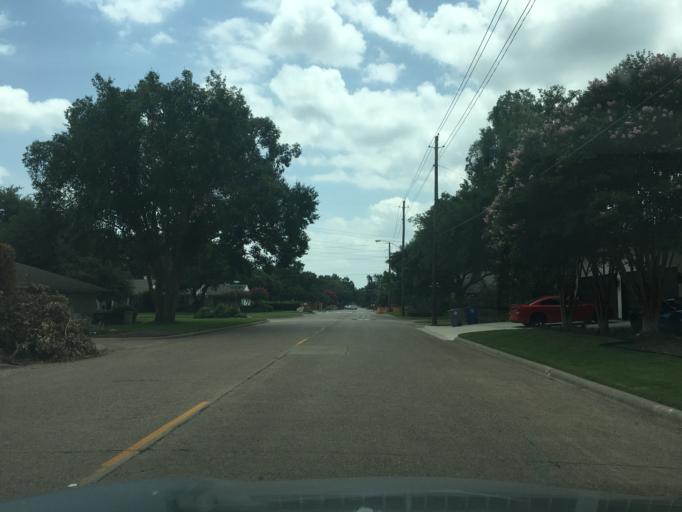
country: US
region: Texas
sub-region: Dallas County
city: Addison
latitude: 32.9042
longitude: -96.8297
